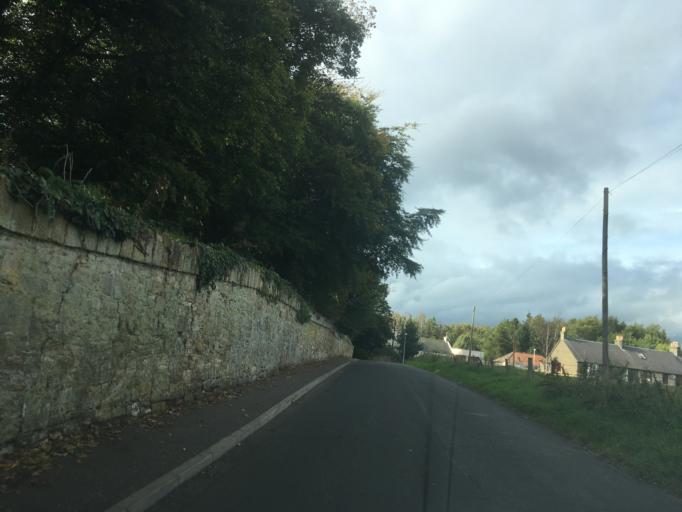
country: GB
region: Scotland
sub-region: East Lothian
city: Musselburgh
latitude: 55.9240
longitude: -3.0435
